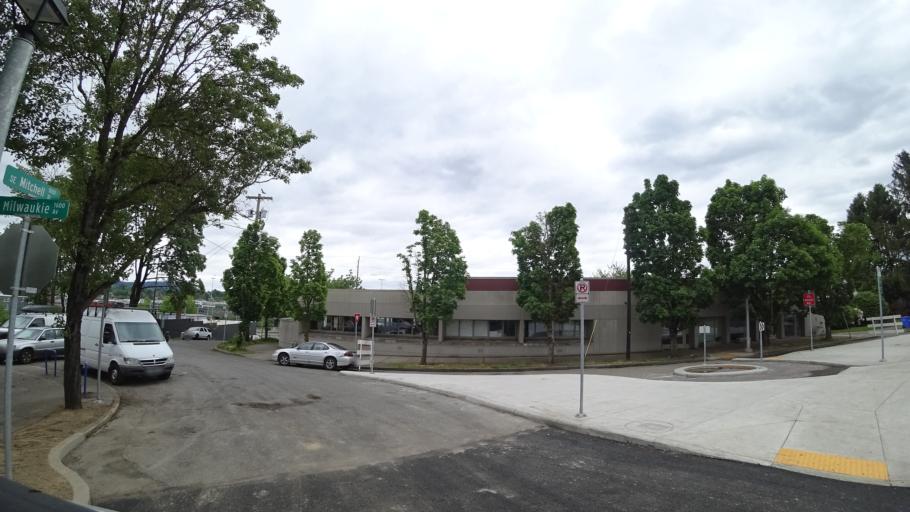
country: US
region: Oregon
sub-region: Clackamas County
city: Milwaukie
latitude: 45.4859
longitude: -122.6497
